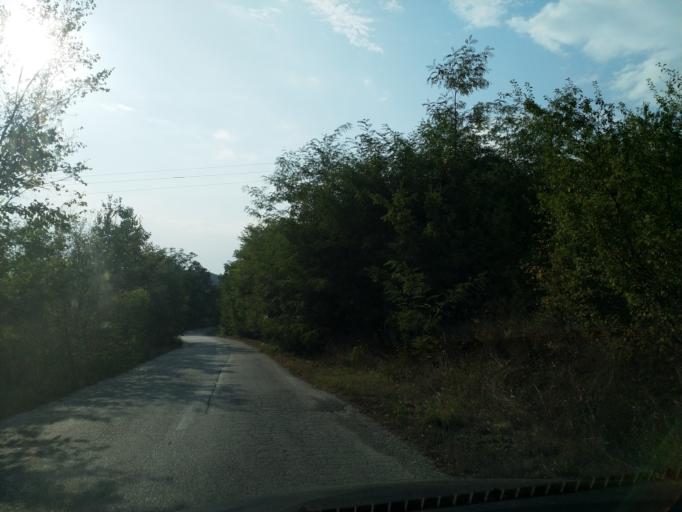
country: RS
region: Central Serbia
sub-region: Pomoravski Okrug
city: Paracin
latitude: 43.8413
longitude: 21.5339
